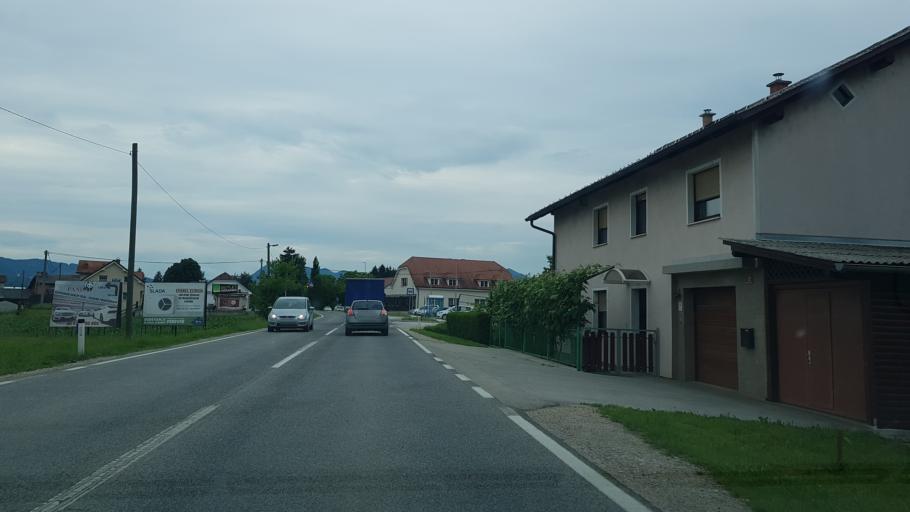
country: SI
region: Celje
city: Trnovlje pri Celju
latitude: 46.2711
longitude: 15.2922
